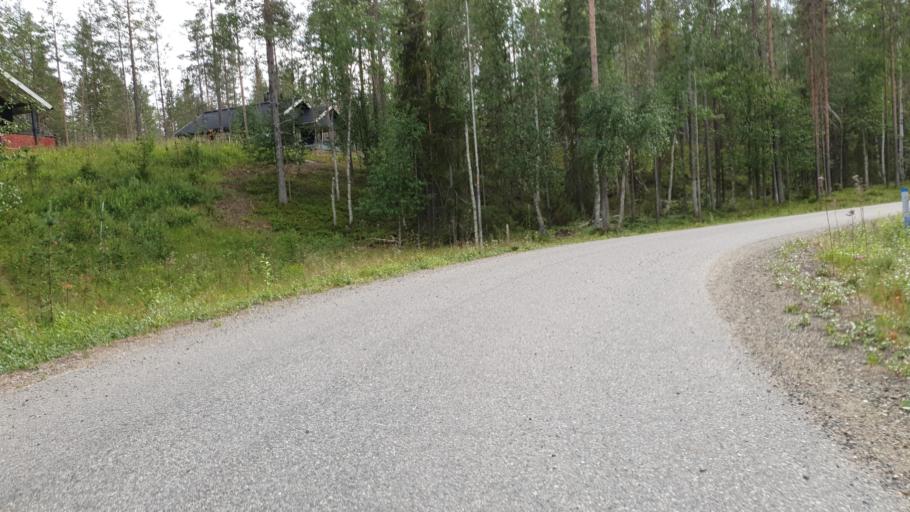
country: FI
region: Lapland
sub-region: Tunturi-Lappi
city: Kolari
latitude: 67.5923
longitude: 24.1299
